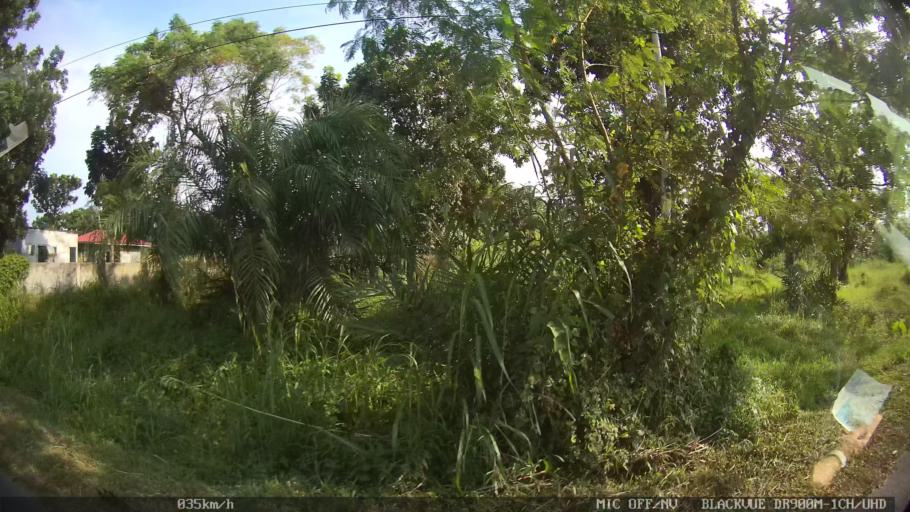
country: ID
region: North Sumatra
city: Percut
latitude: 3.5932
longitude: 98.7979
